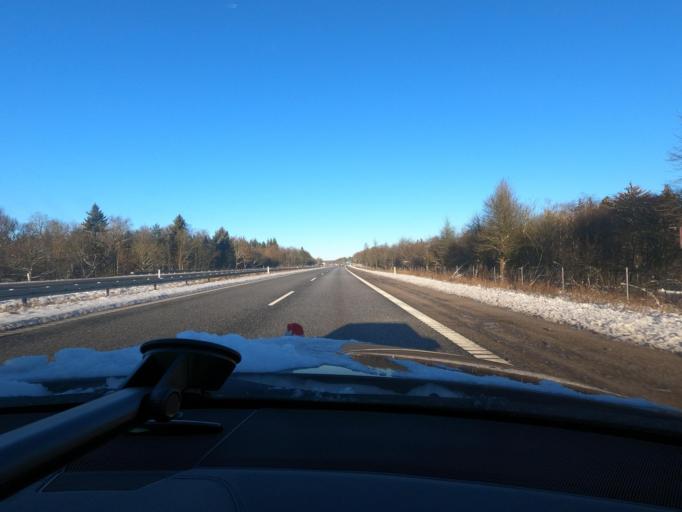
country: DK
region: South Denmark
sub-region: Aabenraa Kommune
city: Aabenraa
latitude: 54.9697
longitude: 9.3820
